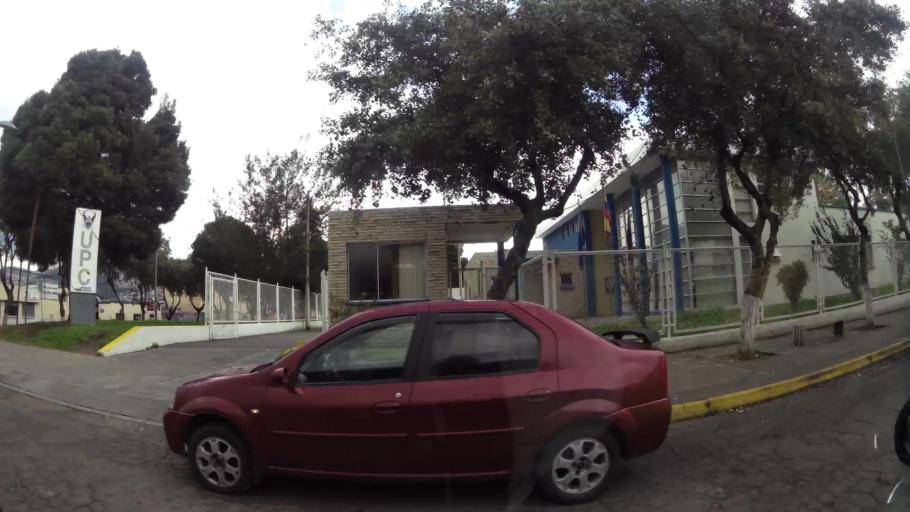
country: EC
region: Pichincha
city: Quito
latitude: -0.2682
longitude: -78.5397
